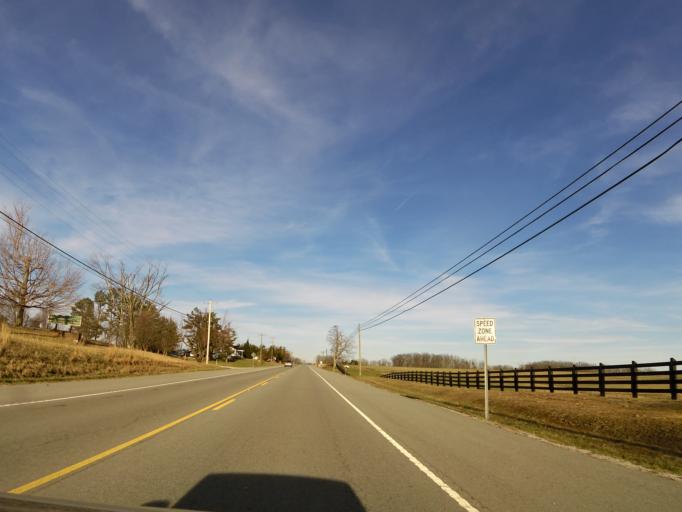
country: US
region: Tennessee
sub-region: White County
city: Sparta
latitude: 35.9390
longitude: -85.3421
